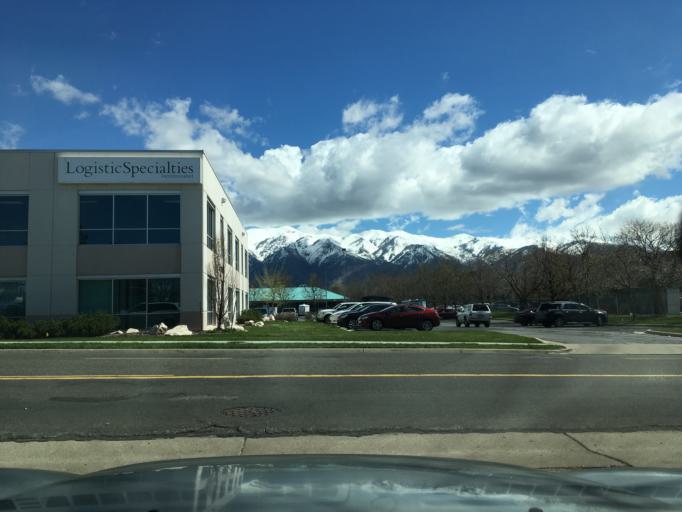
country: US
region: Utah
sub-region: Davis County
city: Layton
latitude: 41.0822
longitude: -111.9785
